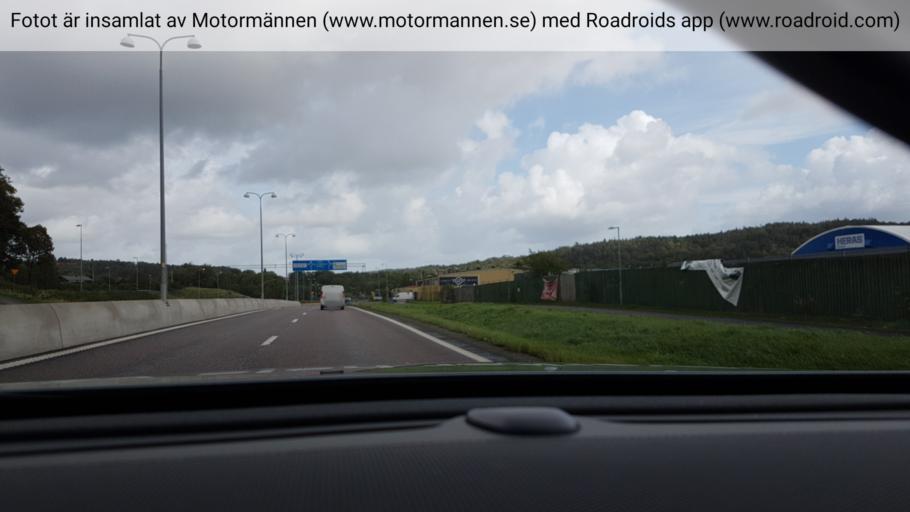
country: SE
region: Vaestra Goetaland
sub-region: Goteborg
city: Eriksbo
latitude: 57.7755
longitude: 12.0604
